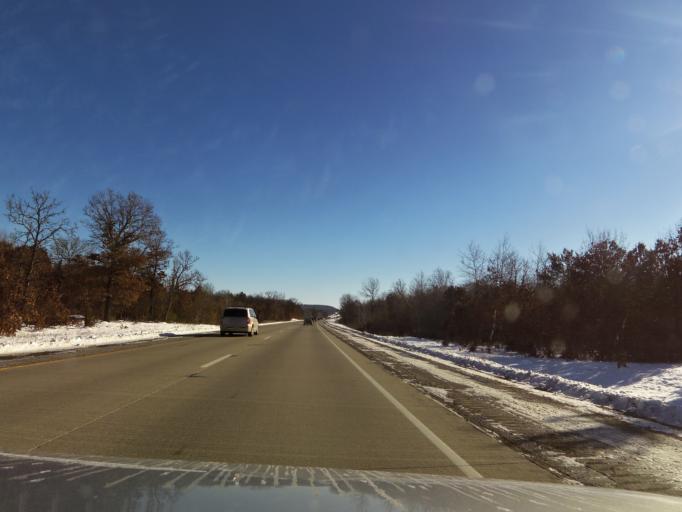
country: US
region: Wisconsin
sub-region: Columbia County
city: Wisconsin Dells
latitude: 43.6914
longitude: -89.8508
